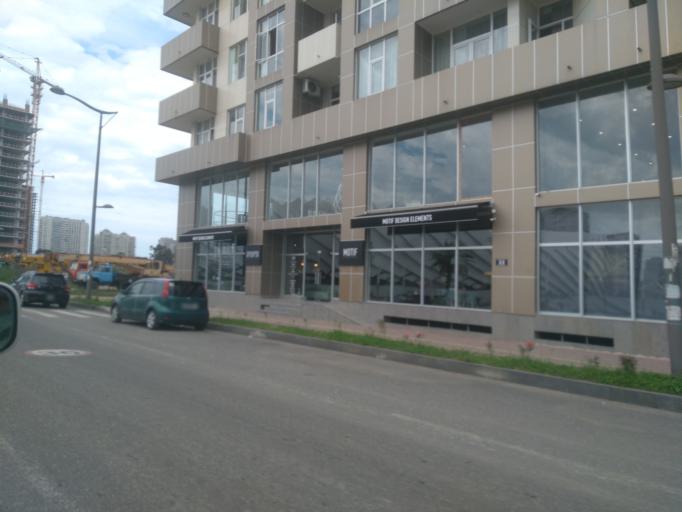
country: GE
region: Ajaria
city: Batumi
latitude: 41.6351
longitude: 41.6222
